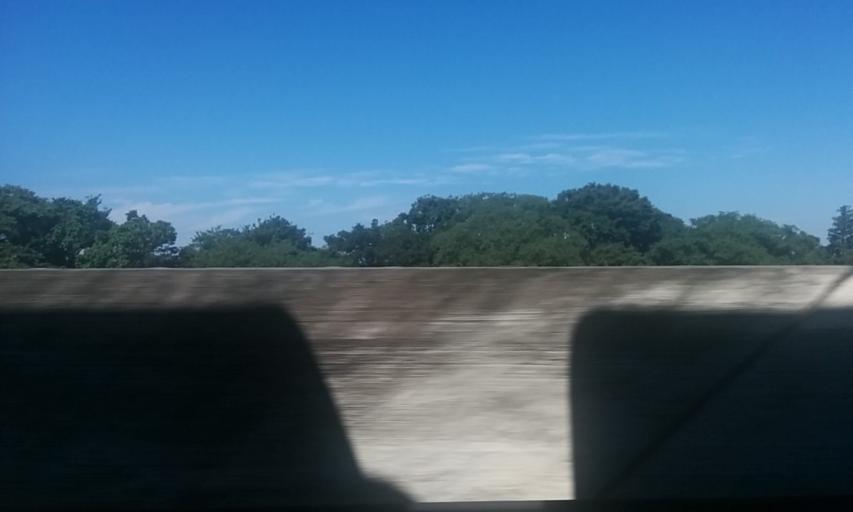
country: JP
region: Ibaraki
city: Moriya
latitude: 35.9164
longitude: 139.9591
